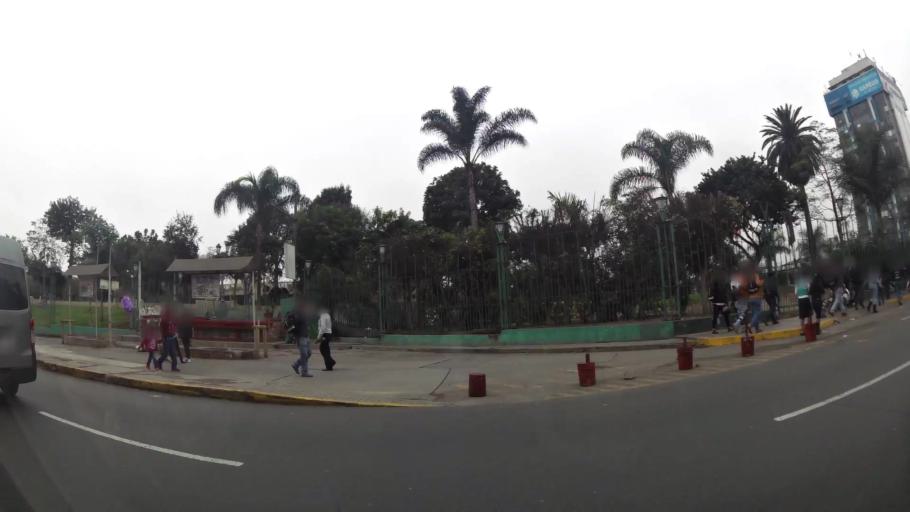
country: PE
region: Lima
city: Lima
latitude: -12.0633
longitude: -77.0343
